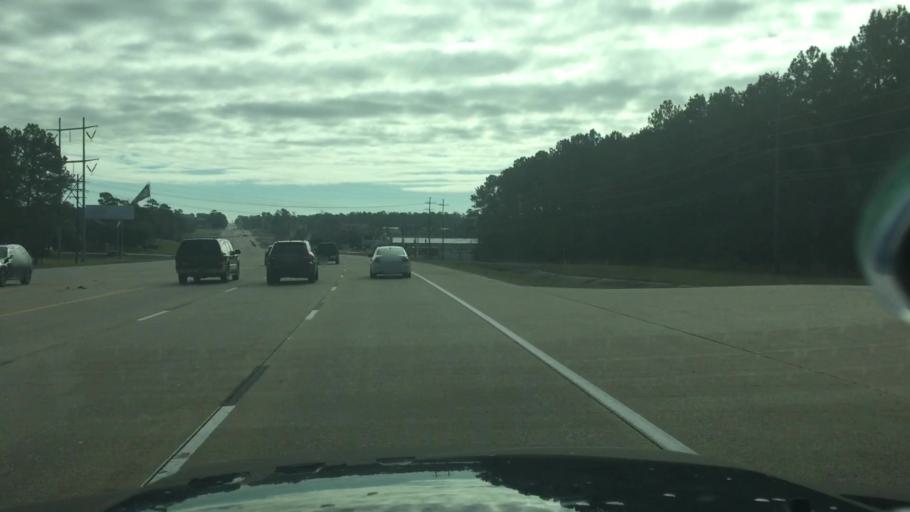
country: US
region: Texas
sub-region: Montgomery County
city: Panorama Village
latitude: 30.3309
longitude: -95.5081
